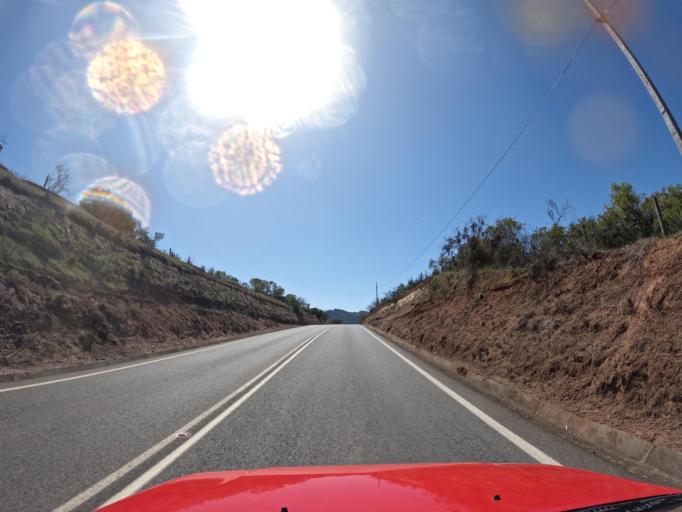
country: CL
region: Maule
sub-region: Provincia de Talca
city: San Clemente
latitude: -35.4515
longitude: -71.2701
